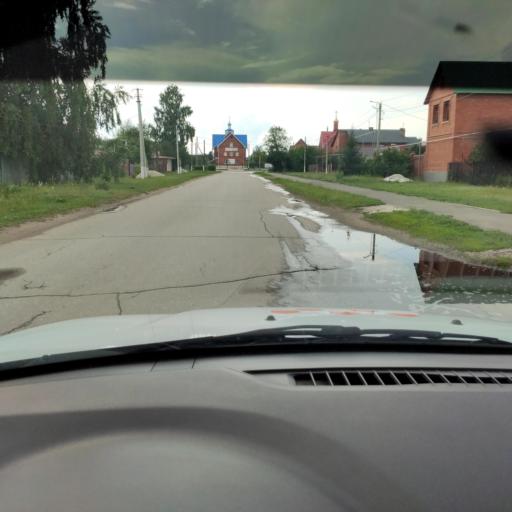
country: RU
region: Samara
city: Podstepki
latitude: 53.6093
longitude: 49.0422
